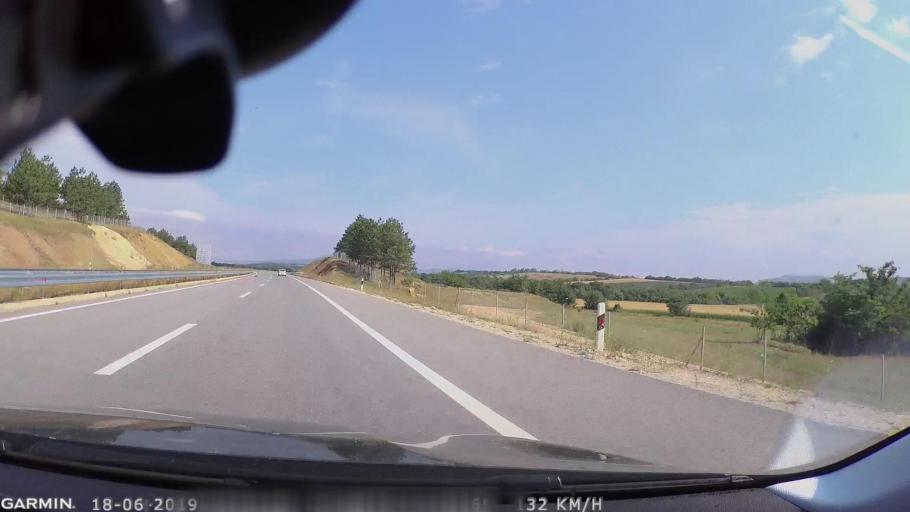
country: MK
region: Sveti Nikole
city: Sveti Nikole
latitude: 41.8886
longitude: 21.9310
